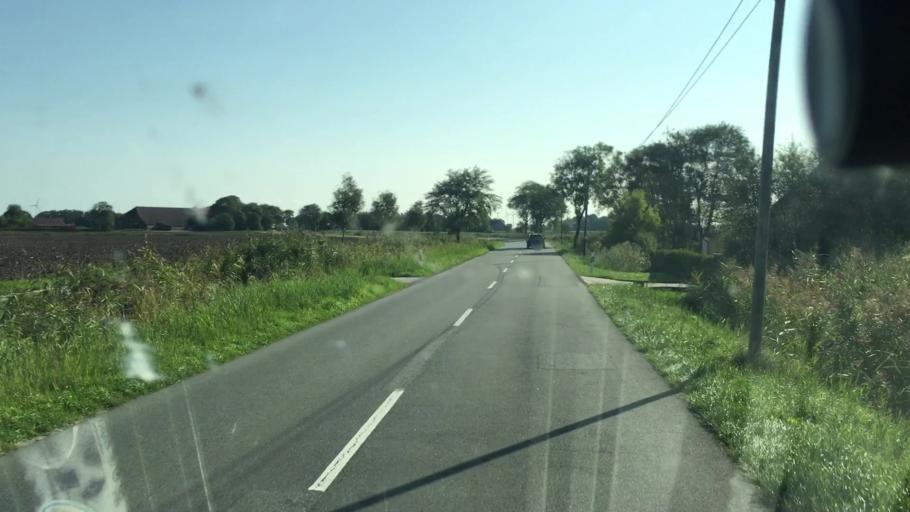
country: DE
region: Lower Saxony
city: Werdum
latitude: 53.6607
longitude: 7.7321
